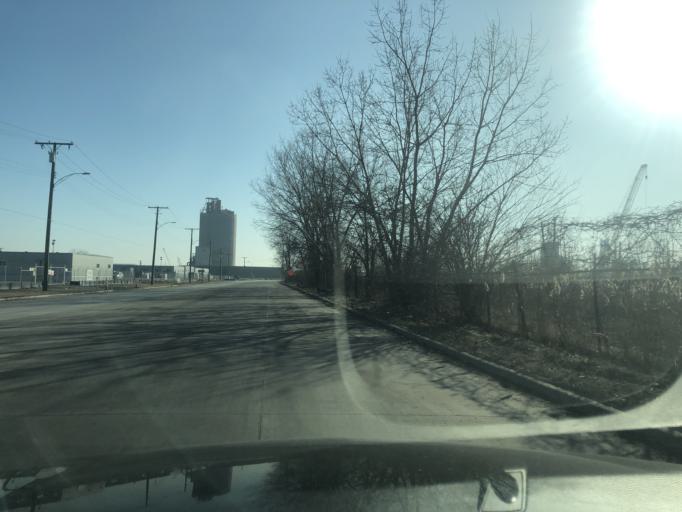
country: US
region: Michigan
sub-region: Wayne County
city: River Rouge
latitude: 42.2953
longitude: -83.1048
